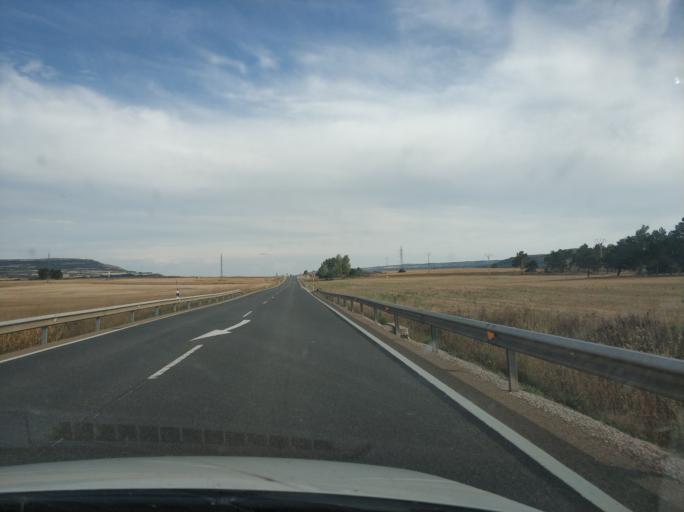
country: ES
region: Castille and Leon
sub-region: Provincia de Palencia
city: Pomar de Valdivia
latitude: 42.7738
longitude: -4.2012
